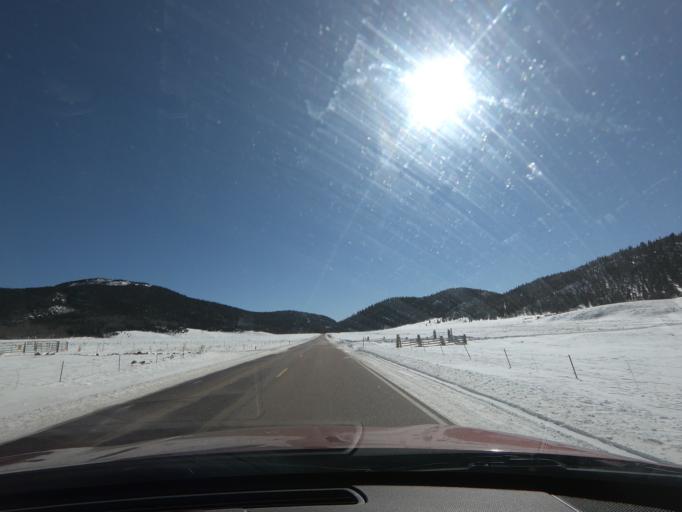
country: US
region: Colorado
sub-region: Teller County
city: Cripple Creek
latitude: 38.7626
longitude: -105.1140
